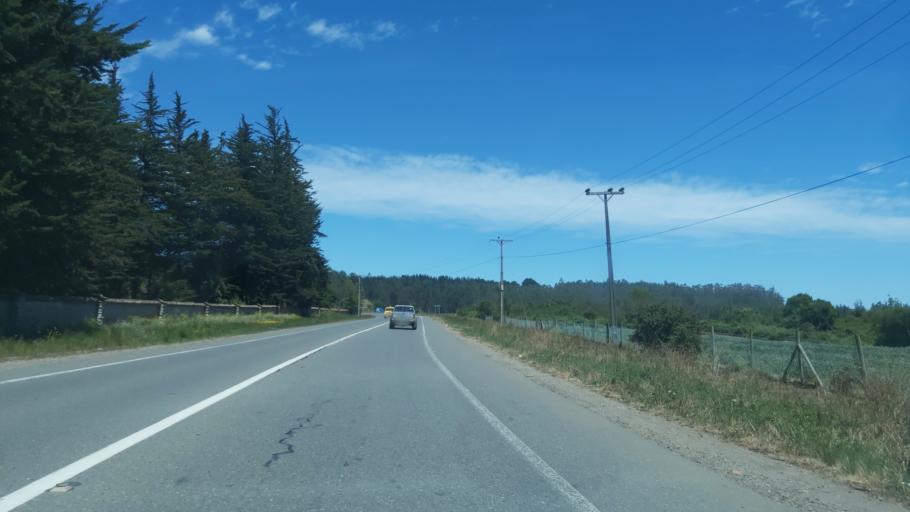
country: CL
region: Maule
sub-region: Provincia de Talca
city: Constitucion
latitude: -35.3121
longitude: -72.3826
